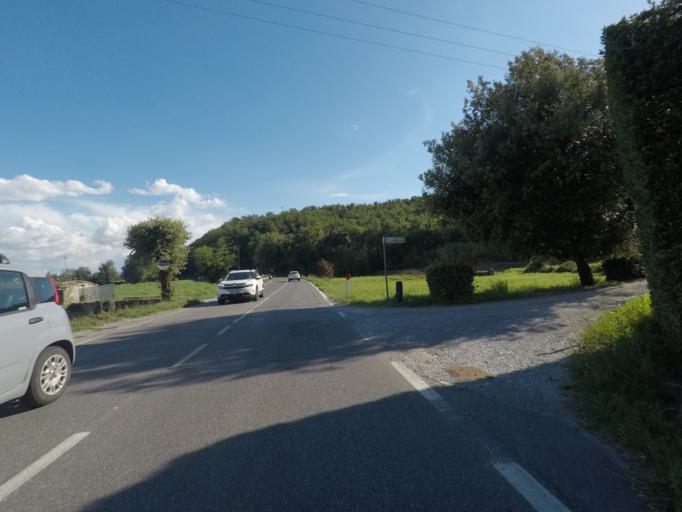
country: IT
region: Tuscany
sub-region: Provincia di Lucca
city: Lucca
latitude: 43.8797
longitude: 10.5209
